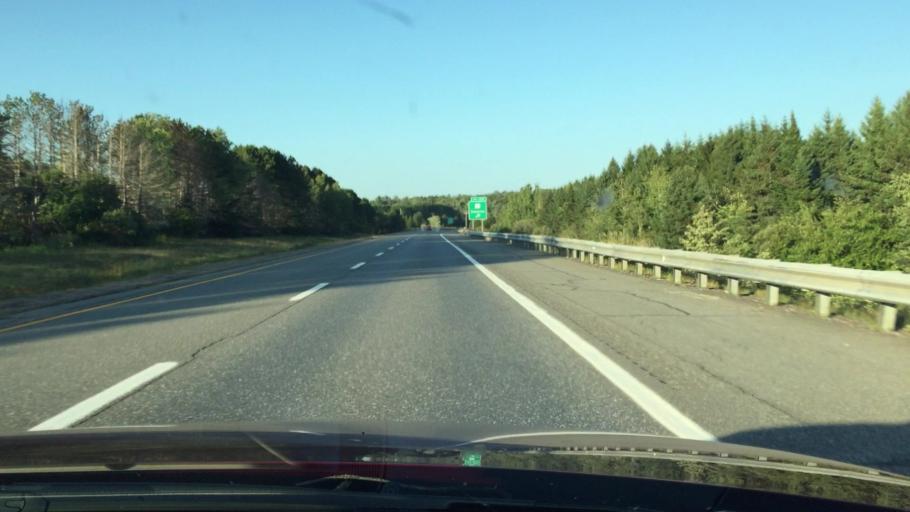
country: US
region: Maine
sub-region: Aroostook County
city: Hodgdon
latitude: 46.1418
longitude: -68.0666
